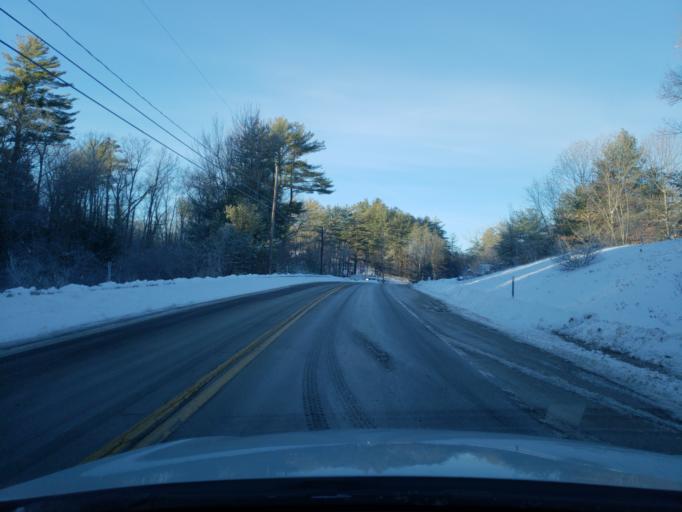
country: US
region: New Hampshire
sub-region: Hillsborough County
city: New Boston
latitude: 42.9812
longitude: -71.6826
